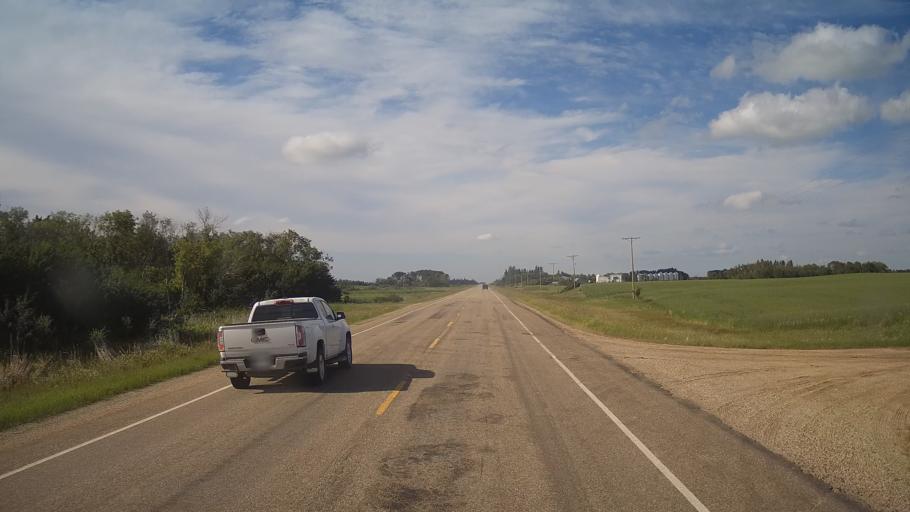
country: CA
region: Saskatchewan
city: Foam Lake
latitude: 51.5829
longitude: -103.8458
